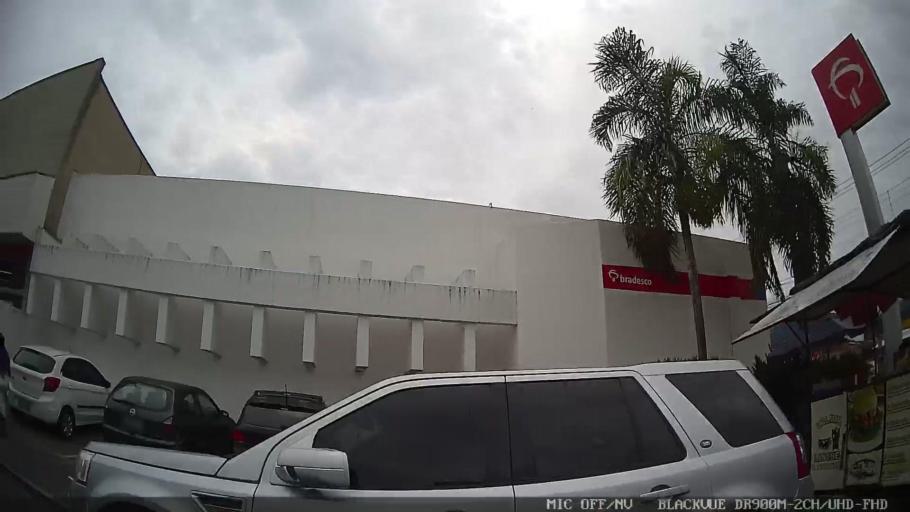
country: BR
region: Sao Paulo
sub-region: Caraguatatuba
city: Caraguatatuba
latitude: -23.6238
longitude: -45.4111
